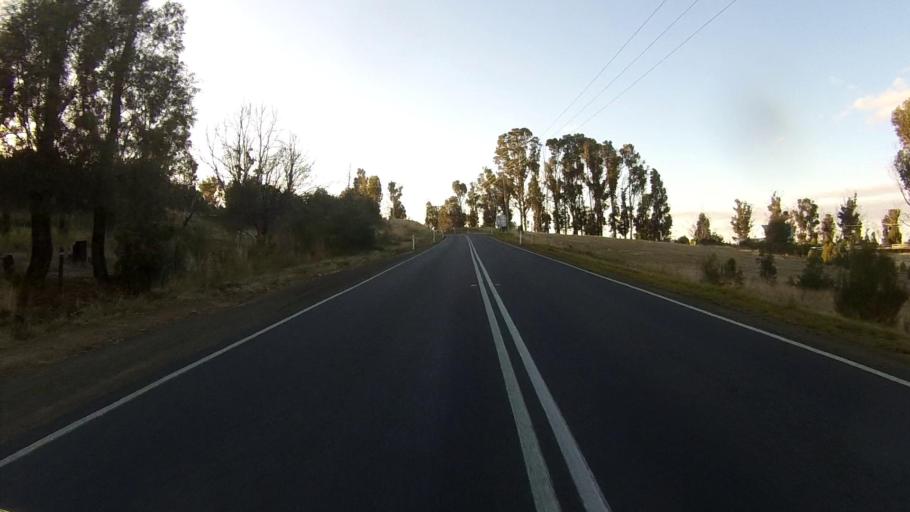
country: AU
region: Tasmania
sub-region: Sorell
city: Sorell
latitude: -42.8747
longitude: 147.8236
